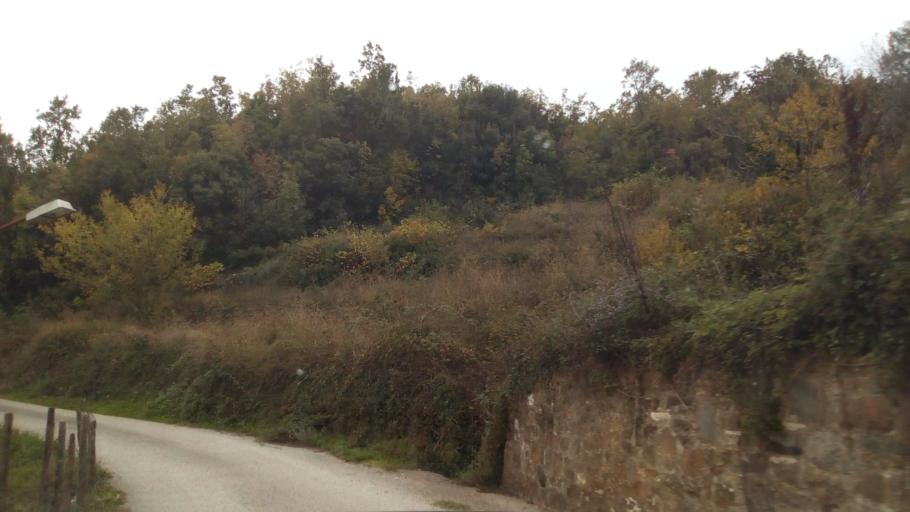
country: GR
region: West Greece
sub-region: Nomos Aitolias kai Akarnanias
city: Thermo
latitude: 38.6053
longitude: 21.8491
